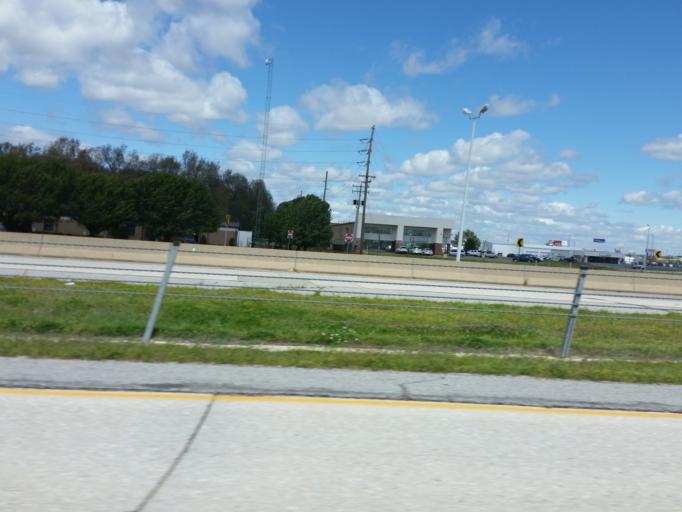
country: US
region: Arkansas
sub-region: Craighead County
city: Jonesboro
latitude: 35.8070
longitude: -90.6805
